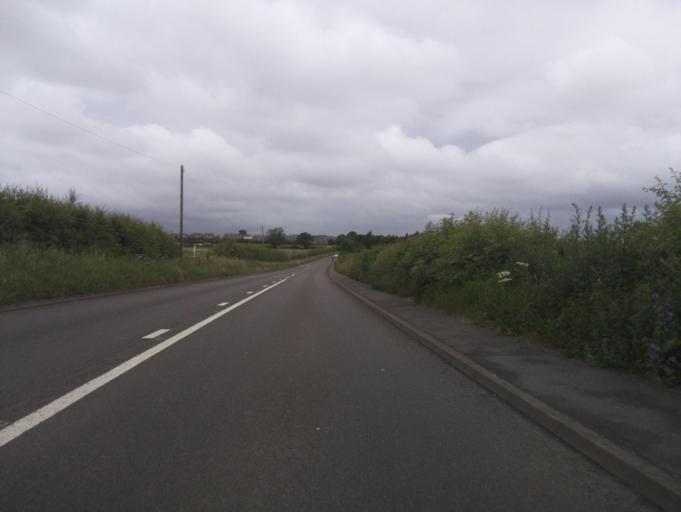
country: GB
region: England
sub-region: Staffordshire
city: Burton upon Trent
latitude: 52.8455
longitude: -1.6761
